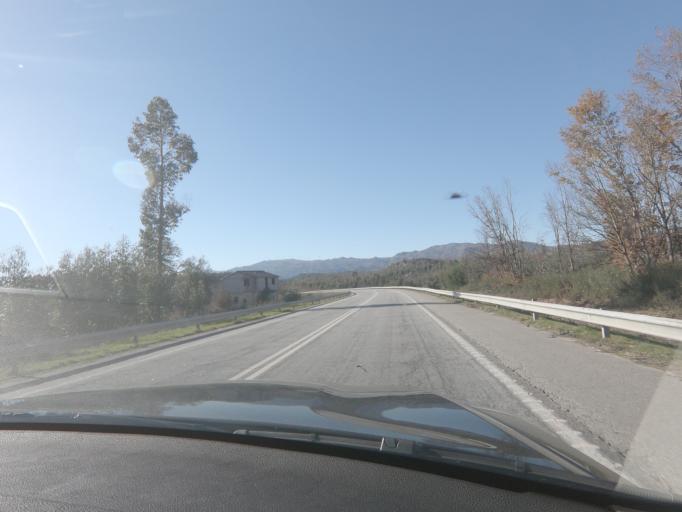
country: PT
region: Viseu
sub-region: Viseu
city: Abraveses
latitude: 40.6548
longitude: -8.0249
